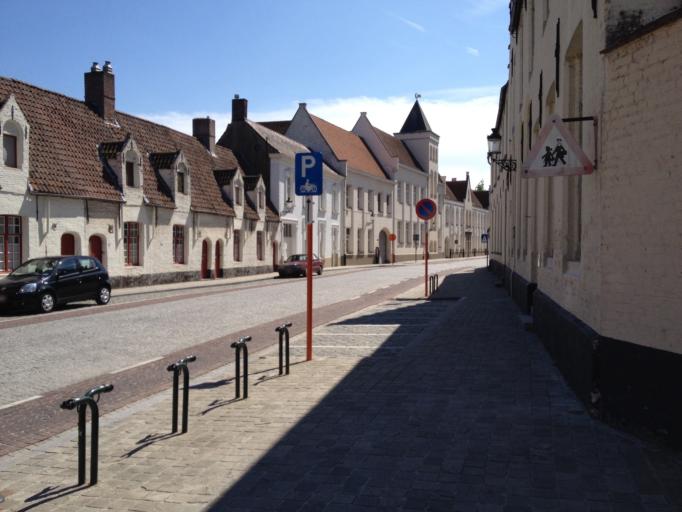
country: BE
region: Flanders
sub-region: Provincie West-Vlaanderen
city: Brugge
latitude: 51.2018
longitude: 3.2157
